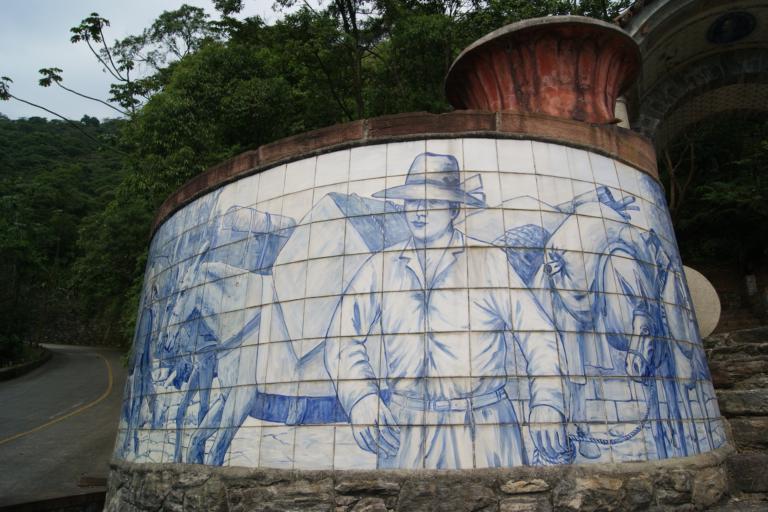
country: BR
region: Sao Paulo
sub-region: Cubatao
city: Cubatao
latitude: -23.8624
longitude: -46.4522
